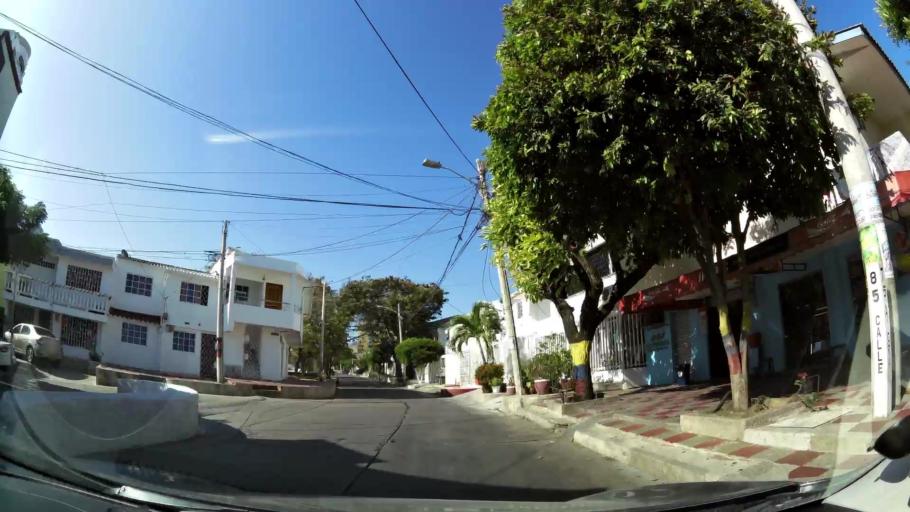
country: CO
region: Atlantico
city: Barranquilla
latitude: 11.0194
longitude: -74.8092
